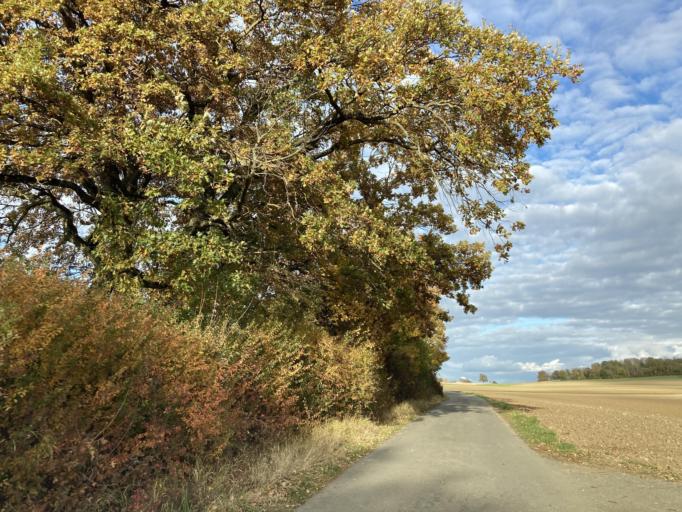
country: DE
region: Baden-Wuerttemberg
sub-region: Tuebingen Region
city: Gomaringen
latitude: 48.4627
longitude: 9.0765
